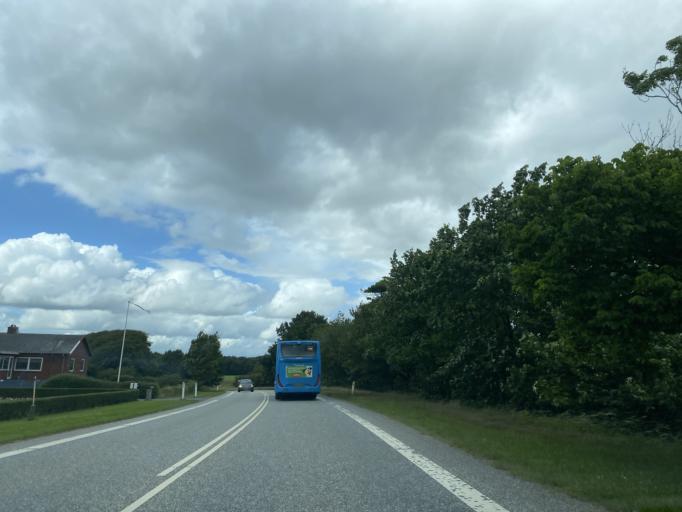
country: DK
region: Central Jutland
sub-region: Silkeborg Kommune
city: Silkeborg
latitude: 56.2542
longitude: 9.6275
